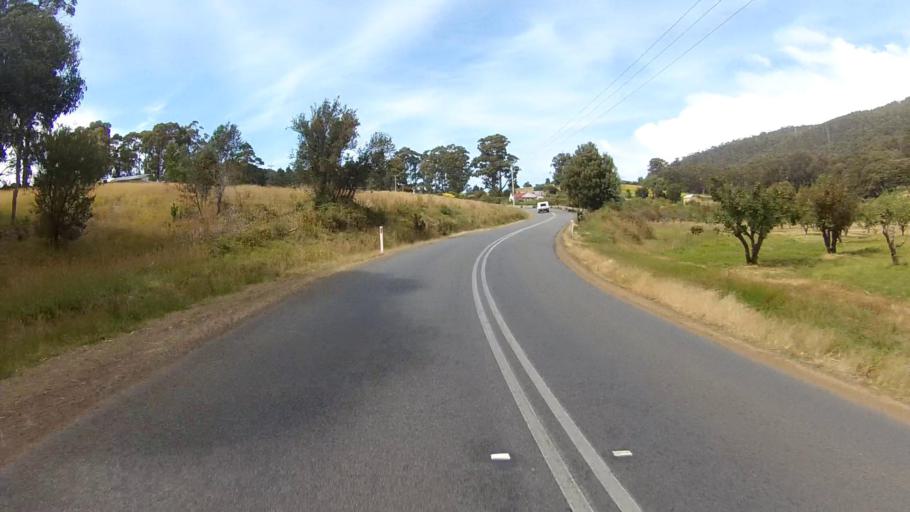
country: AU
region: Tasmania
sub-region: Kingborough
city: Kettering
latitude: -43.1981
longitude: 147.2509
